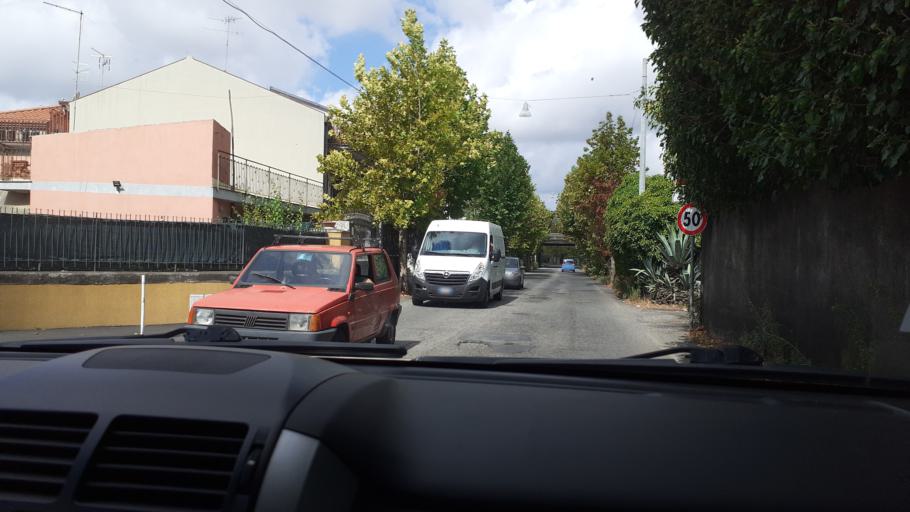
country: IT
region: Sicily
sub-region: Catania
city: San Gregorio di Catania
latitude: 37.5678
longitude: 15.1061
